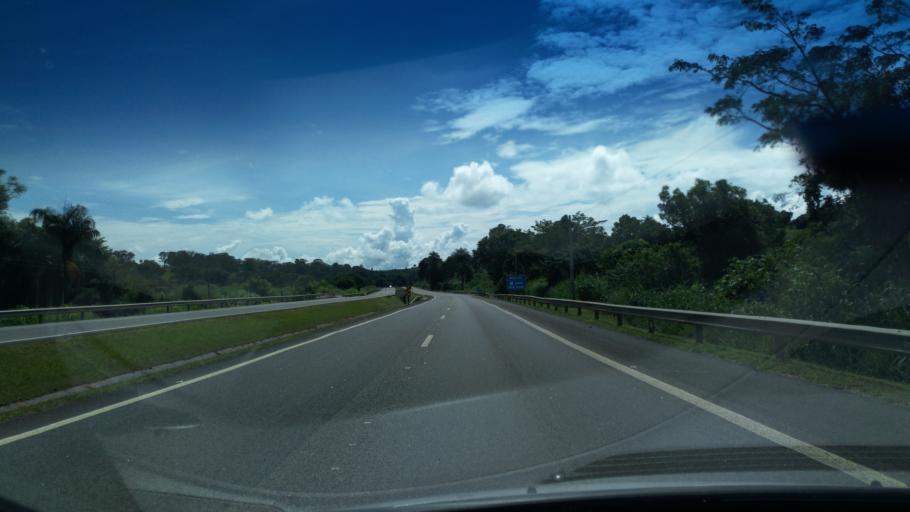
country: BR
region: Sao Paulo
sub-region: Santo Antonio Do Jardim
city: Espirito Santo do Pinhal
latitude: -22.2315
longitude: -46.7961
